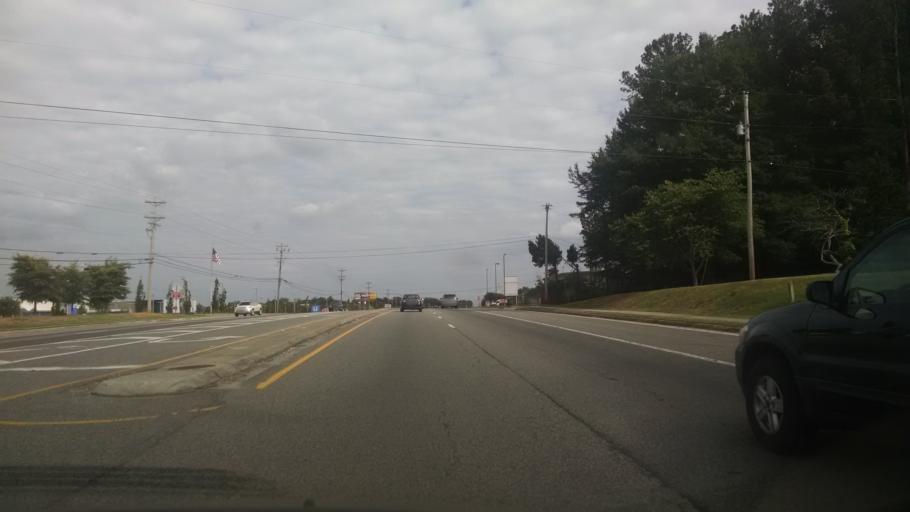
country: US
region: Georgia
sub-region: Forsyth County
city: Cumming
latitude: 34.1770
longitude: -84.1303
